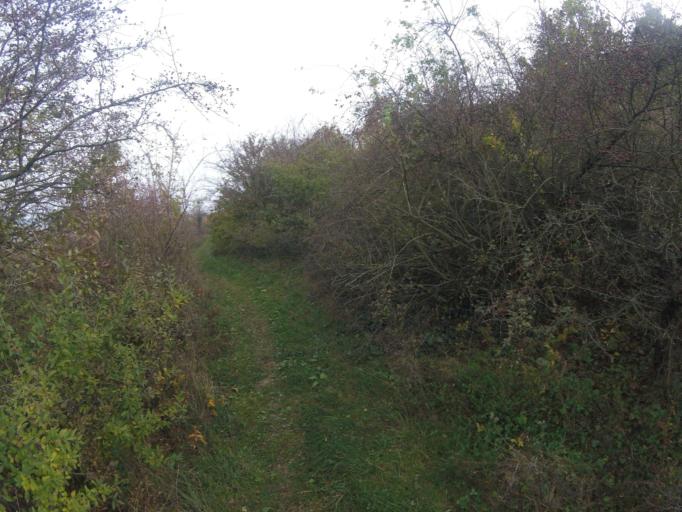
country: HU
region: Fejer
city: Bodajk
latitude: 47.3202
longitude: 18.2155
